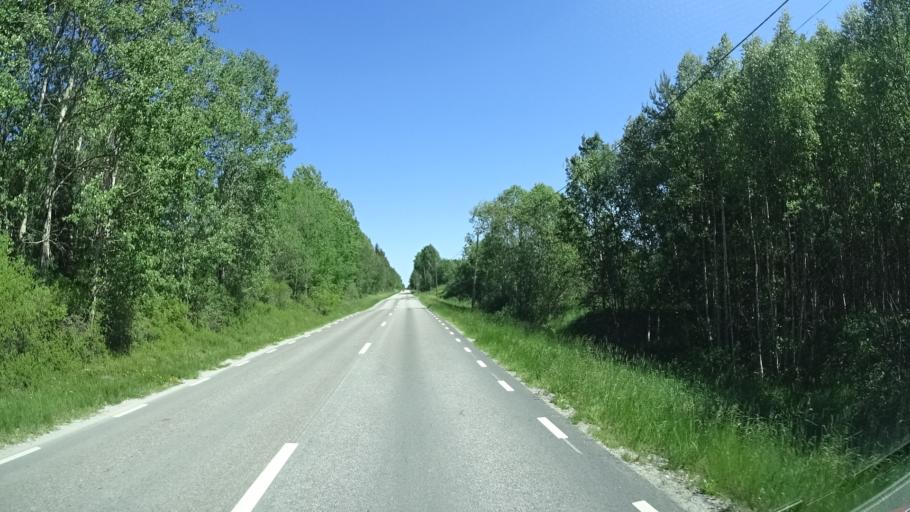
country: SE
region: Stockholm
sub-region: Vallentuna Kommun
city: Vallentuna
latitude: 59.5990
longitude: 18.1222
